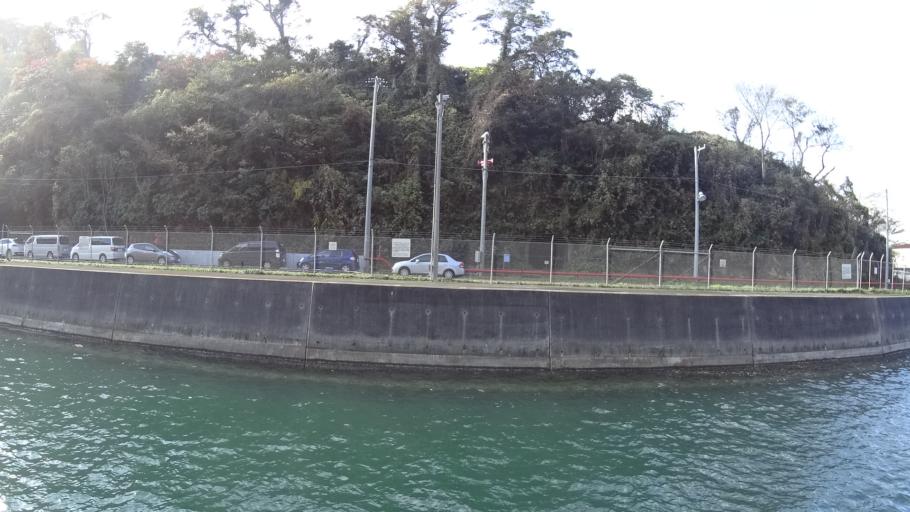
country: JP
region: Kanagawa
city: Yokosuka
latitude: 35.2971
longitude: 139.6456
